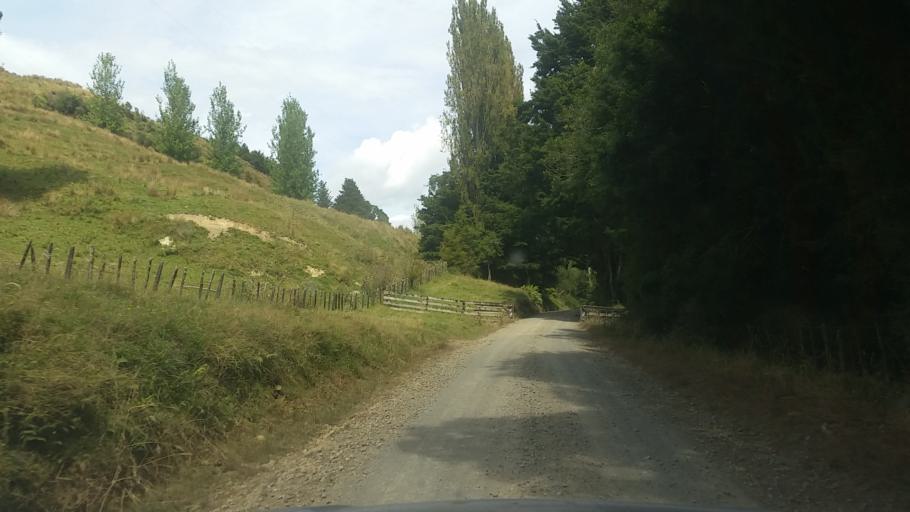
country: NZ
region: Taranaki
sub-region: New Plymouth District
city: Waitara
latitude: -39.0747
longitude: 174.8463
